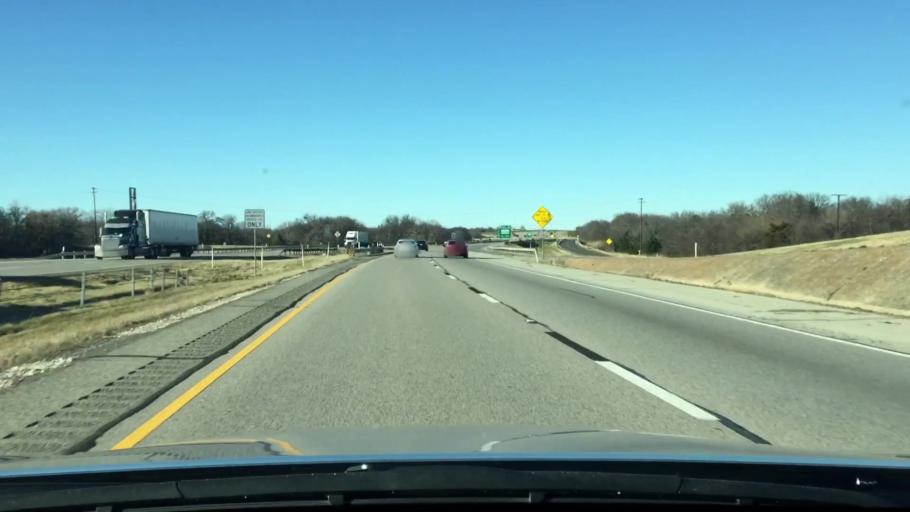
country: US
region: Texas
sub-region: Johnson County
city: Grandview
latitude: 32.2881
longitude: -97.1780
